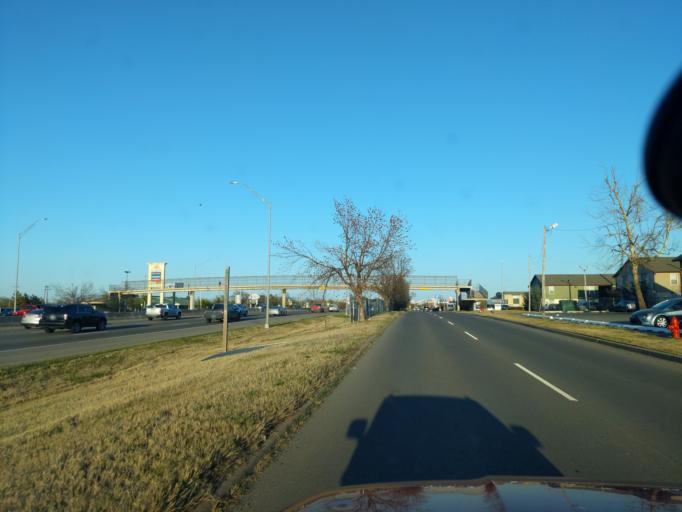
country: US
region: Oklahoma
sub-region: Cleveland County
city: Moore
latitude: 35.3911
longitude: -97.5409
